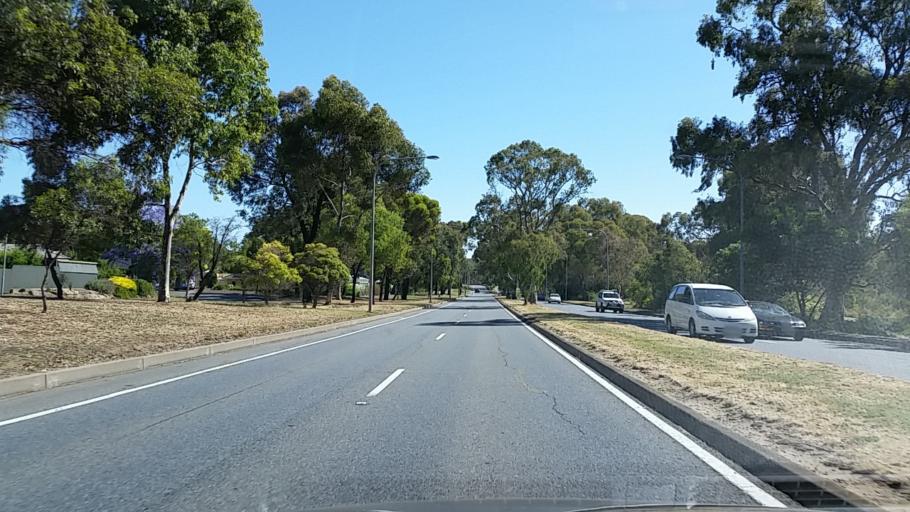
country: AU
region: South Australia
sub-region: Tea Tree Gully
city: Hope Valley
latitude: -34.8106
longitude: 138.6964
